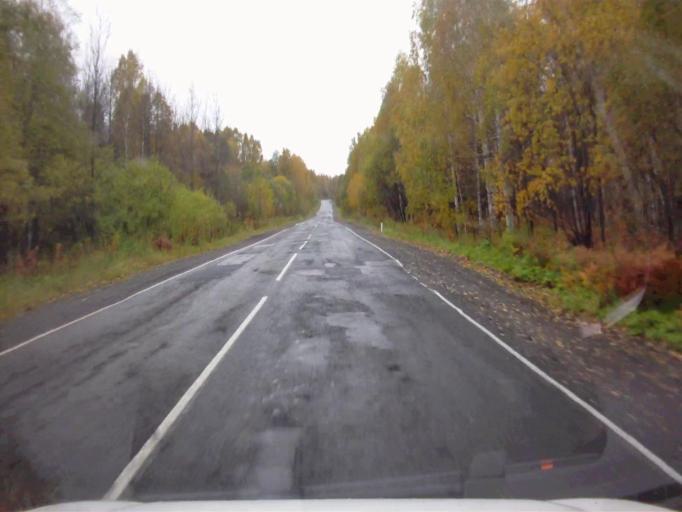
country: RU
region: Chelyabinsk
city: Nizhniy Ufaley
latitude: 56.0548
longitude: 60.0491
